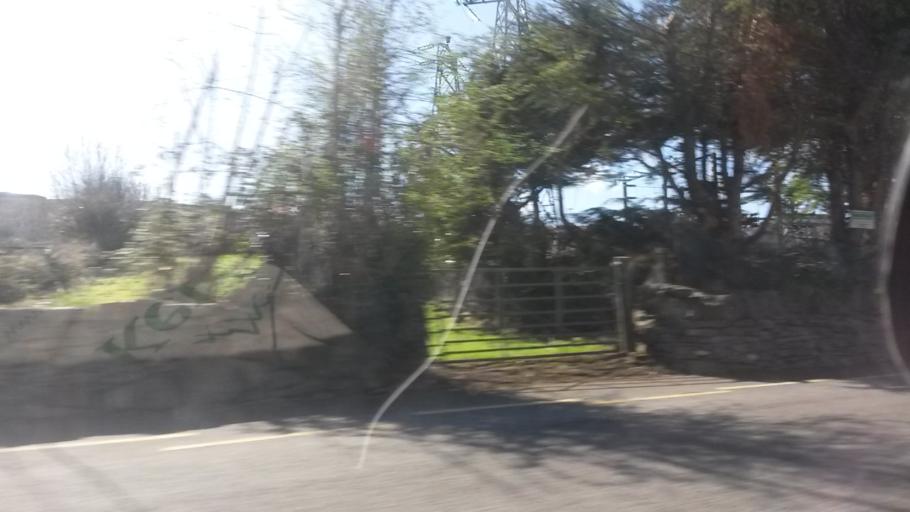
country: IE
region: Munster
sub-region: Ciarrai
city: Kenmare
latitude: 51.9040
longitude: -9.4355
